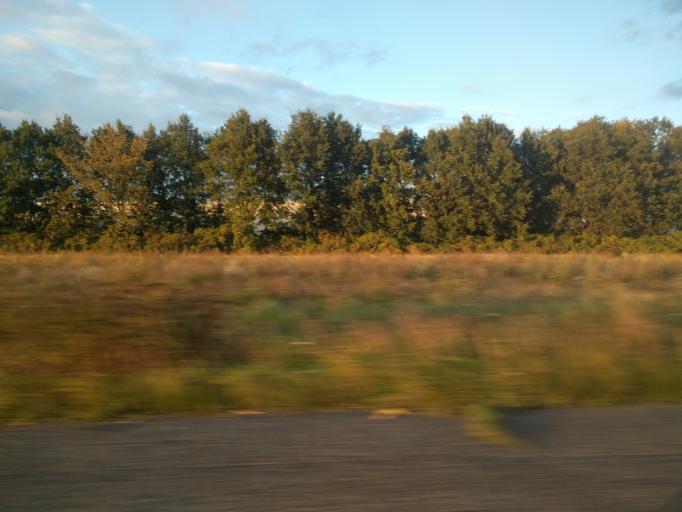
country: DK
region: South Denmark
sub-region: Nyborg Kommune
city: Ullerslev
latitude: 55.3530
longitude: 10.6190
